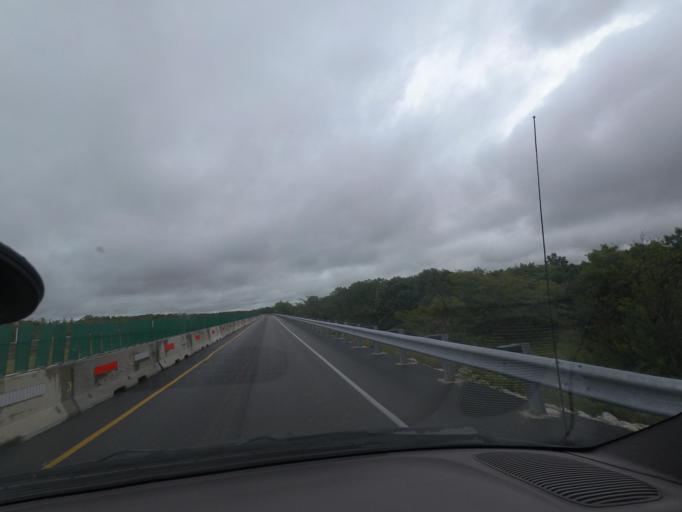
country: US
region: Illinois
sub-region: Piatt County
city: Cerro Gordo
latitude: 39.9767
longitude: -88.7983
